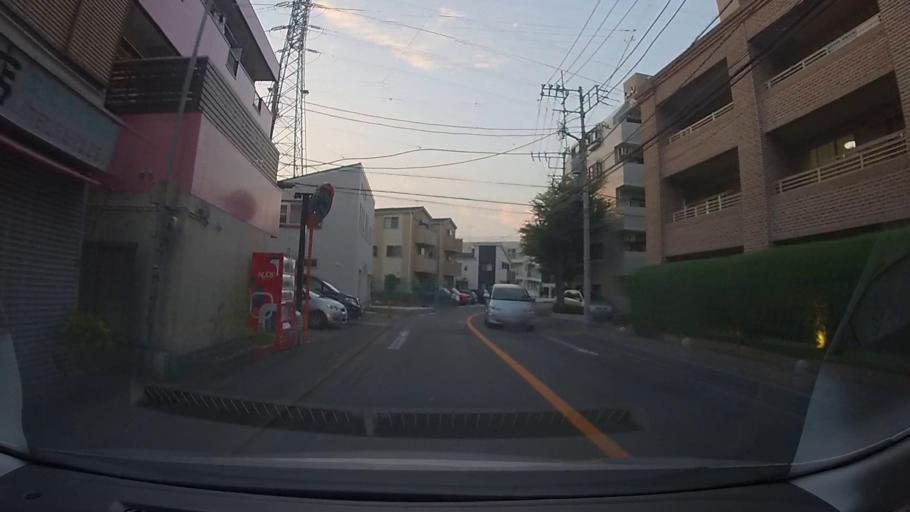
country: JP
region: Kanagawa
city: Minami-rinkan
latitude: 35.5012
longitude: 139.4433
